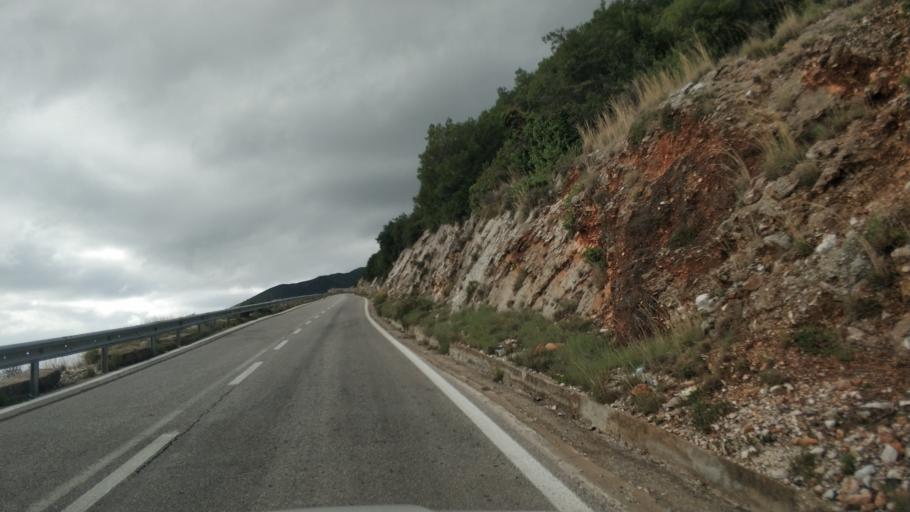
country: AL
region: Vlore
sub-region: Rrethi i Vlores
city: Vranisht
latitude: 40.1786
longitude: 19.5977
